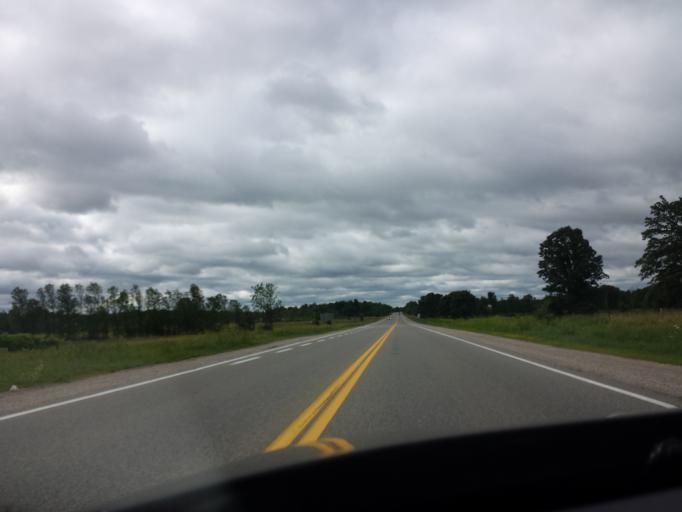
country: CA
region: Ontario
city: Perth
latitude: 44.9928
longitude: -76.2282
